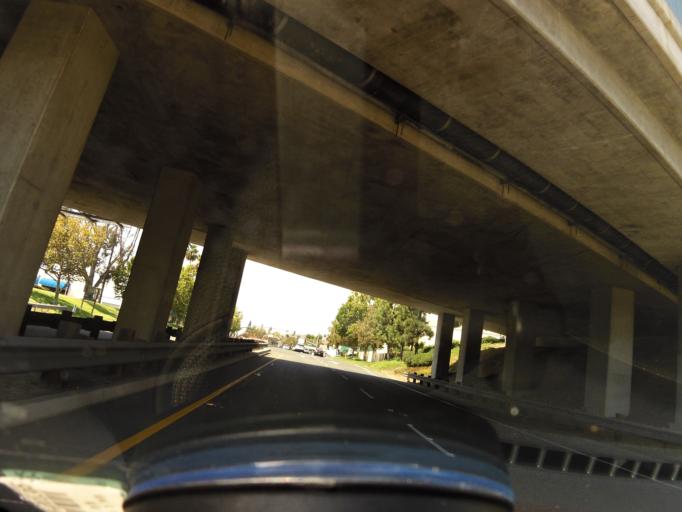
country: US
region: California
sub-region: Orange County
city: Yorba Linda
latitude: 33.8870
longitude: -117.8124
